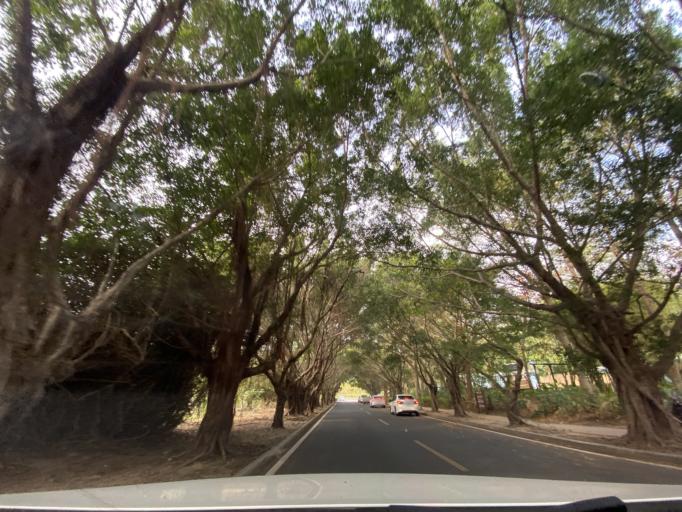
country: CN
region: Hainan
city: Tiandu
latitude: 18.2264
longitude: 109.6211
